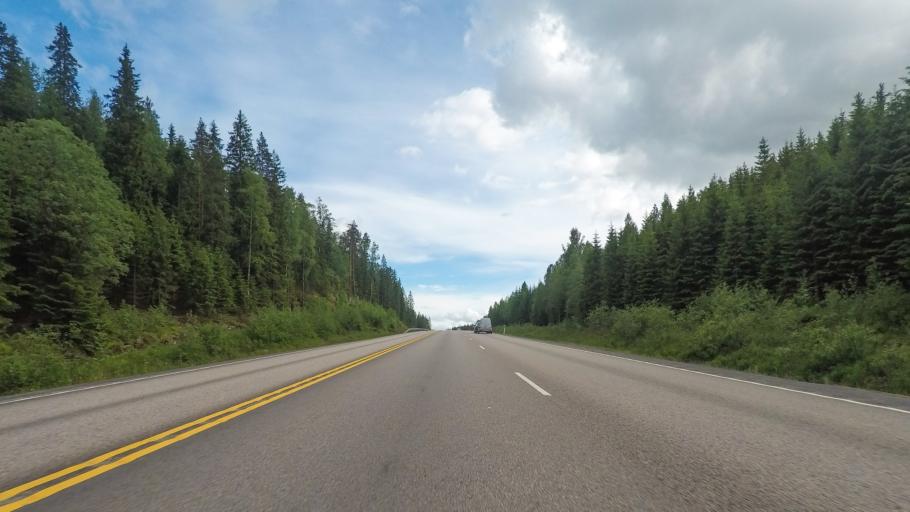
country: FI
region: Central Finland
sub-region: Jyvaeskylae
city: Toivakka
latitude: 62.0477
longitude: 26.0517
